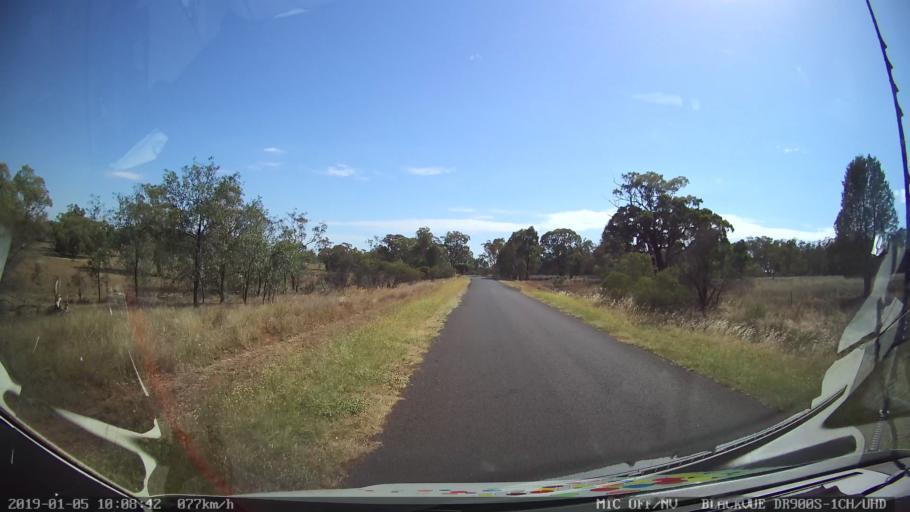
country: AU
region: New South Wales
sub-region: Gilgandra
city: Gilgandra
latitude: -31.6384
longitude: 148.8813
